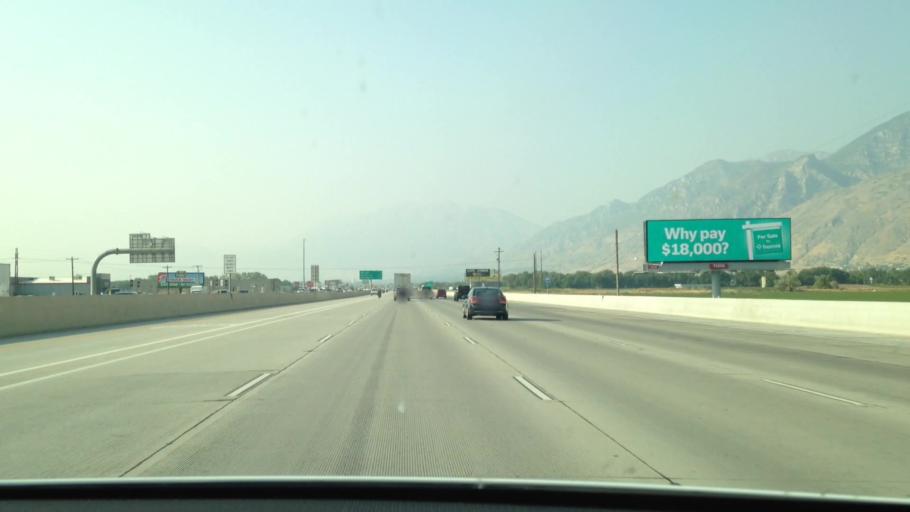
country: US
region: Utah
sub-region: Utah County
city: Springville
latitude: 40.1708
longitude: -111.6465
